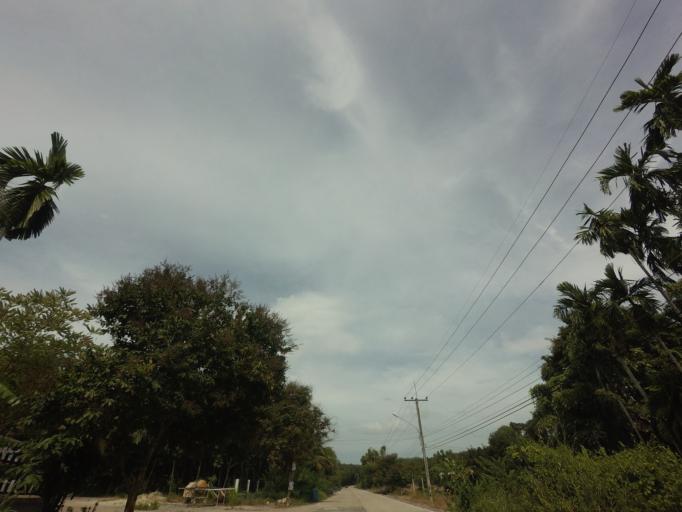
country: TH
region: Rayong
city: Klaeng
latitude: 12.6550
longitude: 101.5620
